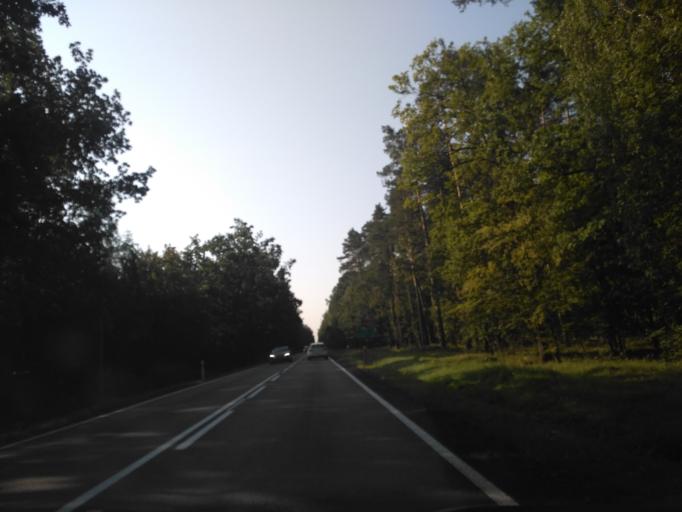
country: PL
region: Subcarpathian Voivodeship
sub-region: Powiat nizanski
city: Nisko
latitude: 50.4937
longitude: 22.1384
